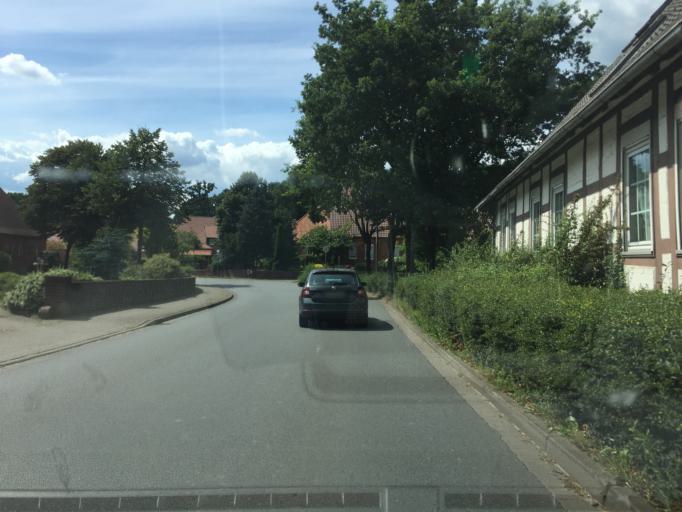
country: DE
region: Lower Saxony
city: Bohme
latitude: 52.8209
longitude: 9.4550
